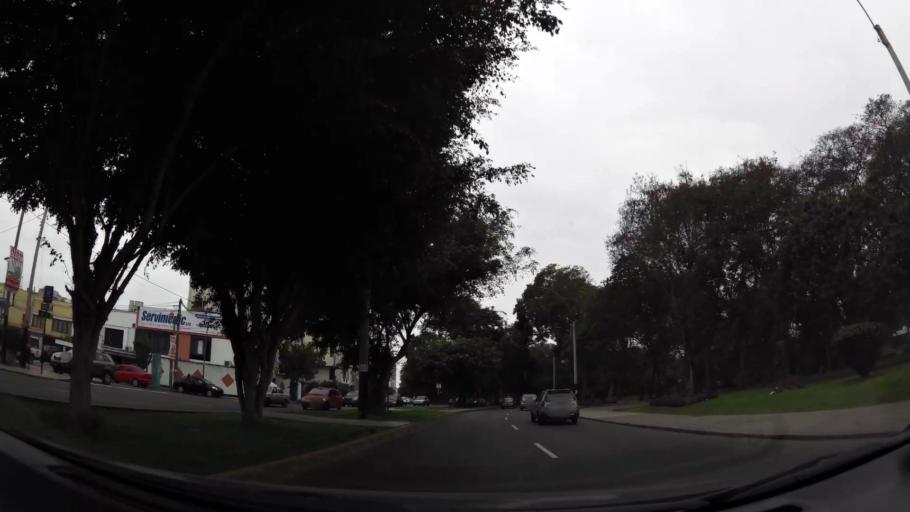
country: PE
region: Lima
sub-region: Lima
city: San Isidro
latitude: -12.0891
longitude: -77.0390
